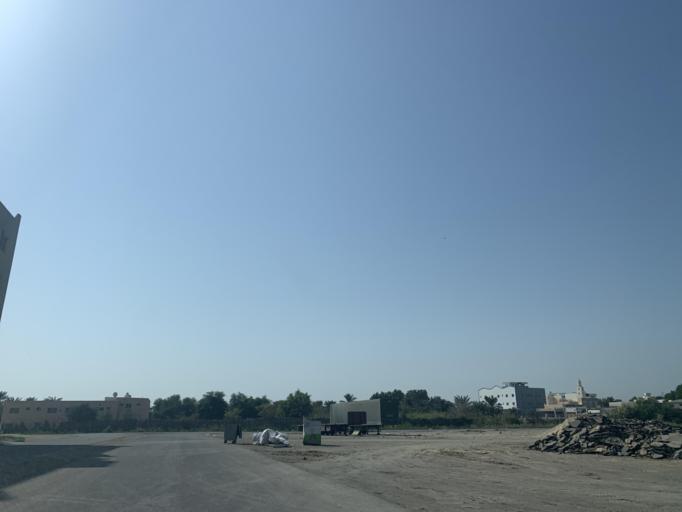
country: BH
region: Central Governorate
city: Madinat Hamad
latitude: 26.1368
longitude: 50.4876
